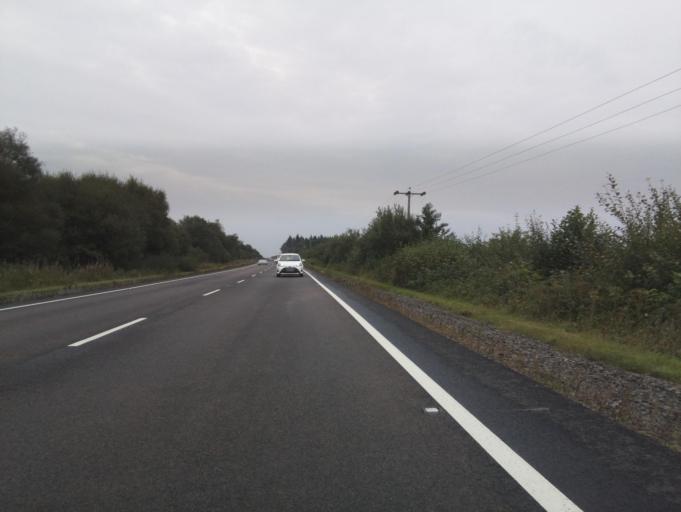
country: GB
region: Scotland
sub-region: Dumfries and Galloway
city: Gretna
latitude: 54.9918
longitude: -3.1584
